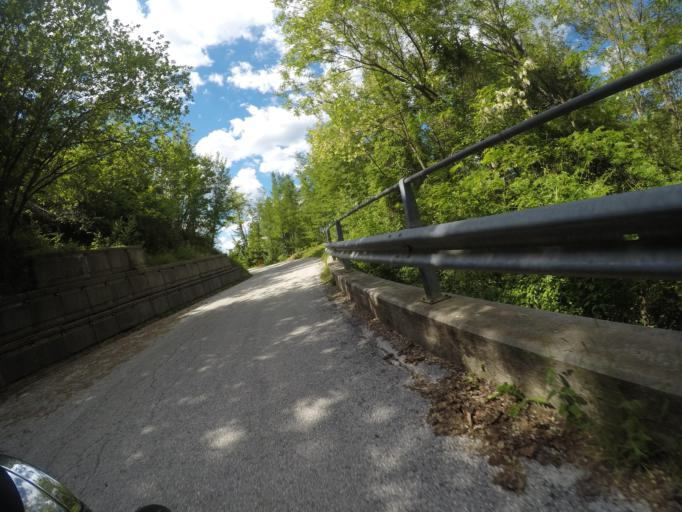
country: IT
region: Tuscany
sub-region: Provincia di Lucca
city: Minucciano
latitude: 44.1656
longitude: 10.2088
